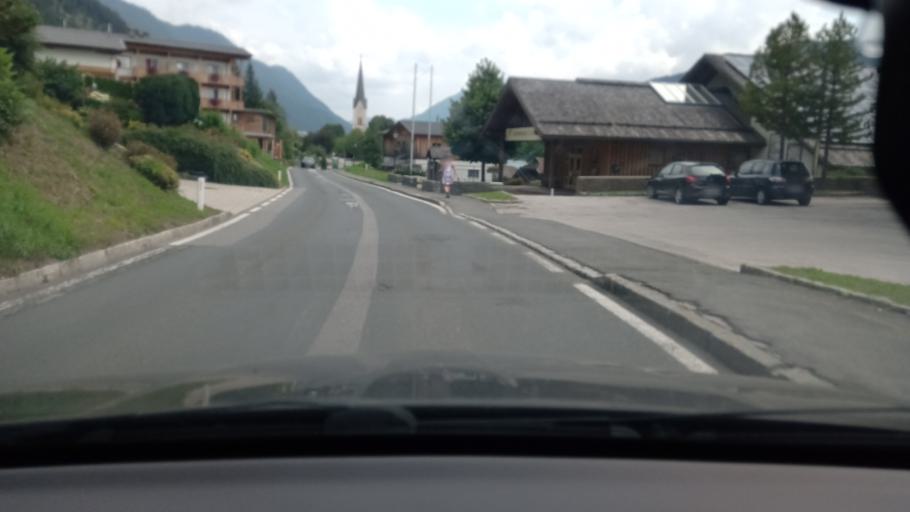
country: AT
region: Carinthia
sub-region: Politischer Bezirk Spittal an der Drau
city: Steinfeld
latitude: 46.7189
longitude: 13.2861
